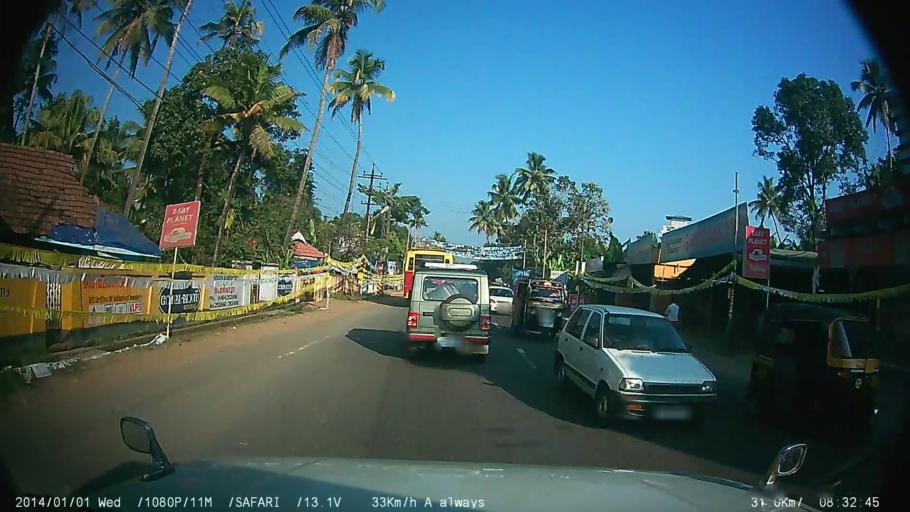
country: IN
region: Kerala
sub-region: Ernakulam
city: Perumpavur
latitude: 10.1189
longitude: 76.4745
